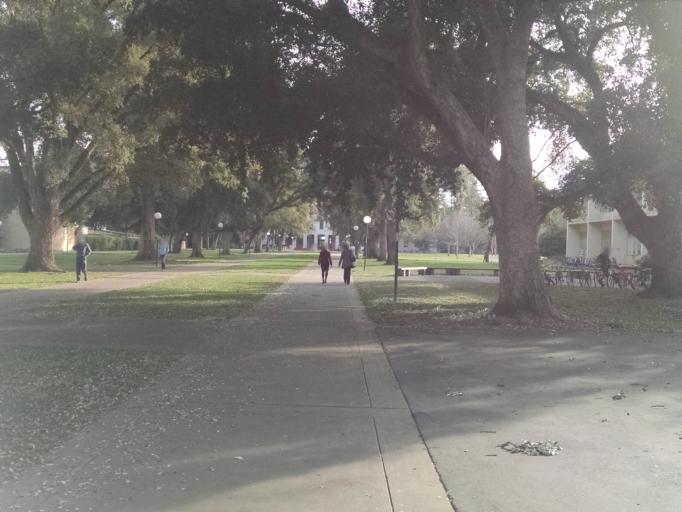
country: US
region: California
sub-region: Yolo County
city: Davis
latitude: 38.5389
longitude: -121.7498
